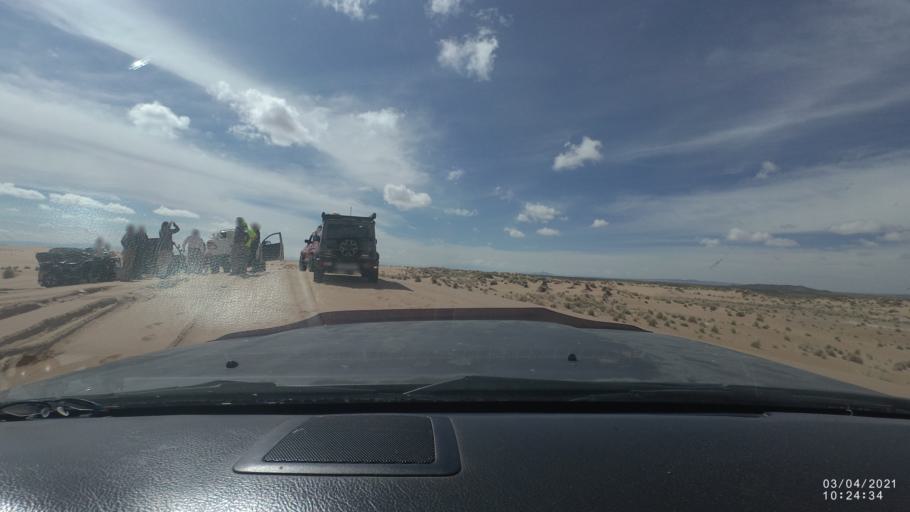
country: BO
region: Oruro
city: Poopo
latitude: -18.7063
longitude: -67.5231
